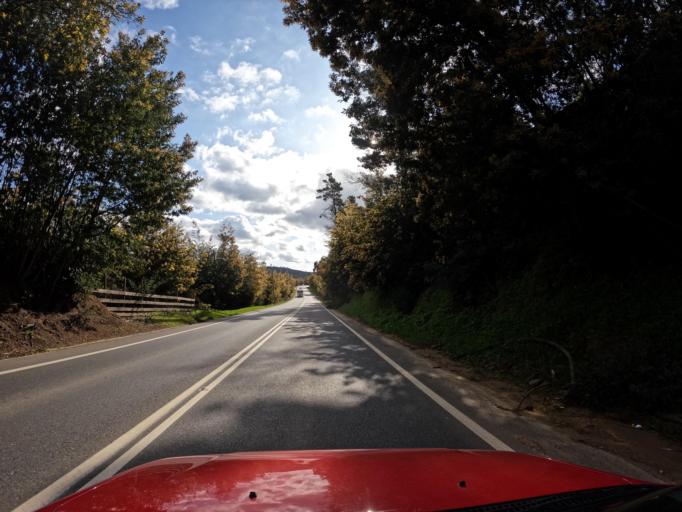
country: CL
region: Maule
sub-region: Provincia de Talca
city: Constitucion
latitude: -35.5375
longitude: -72.1612
